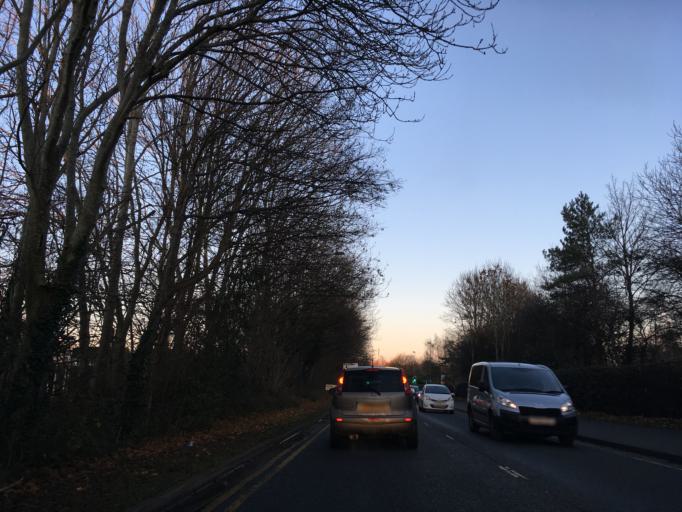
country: GB
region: England
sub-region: South Gloucestershire
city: Stoke Gifford
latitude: 51.5126
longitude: -2.5489
